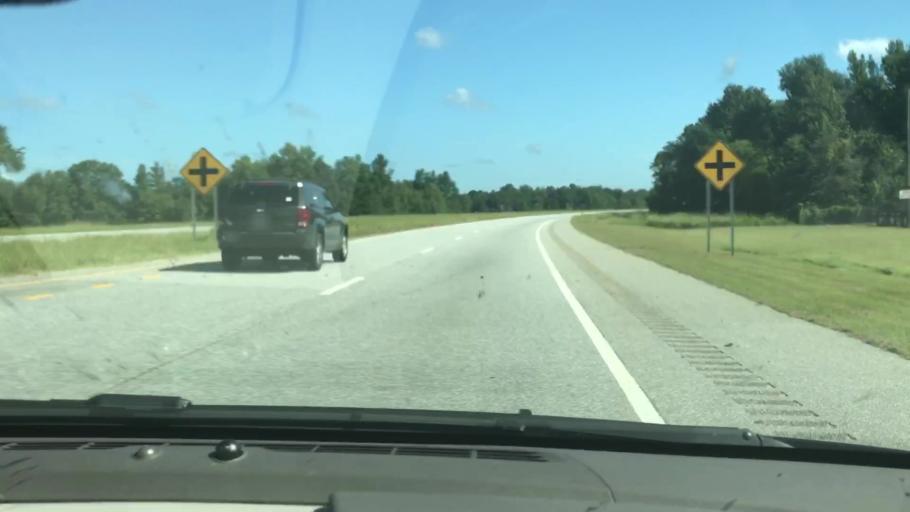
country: US
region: Alabama
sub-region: Russell County
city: Ladonia
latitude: 32.1917
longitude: -85.1813
